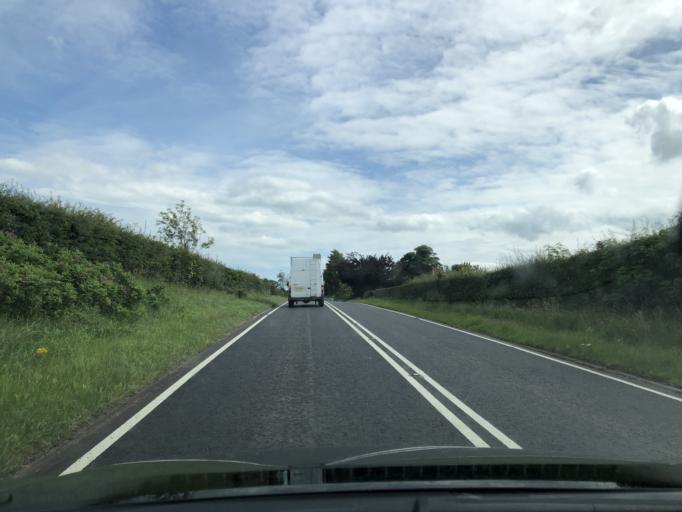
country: GB
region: Northern Ireland
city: Annahilt
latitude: 54.4383
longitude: -5.9384
